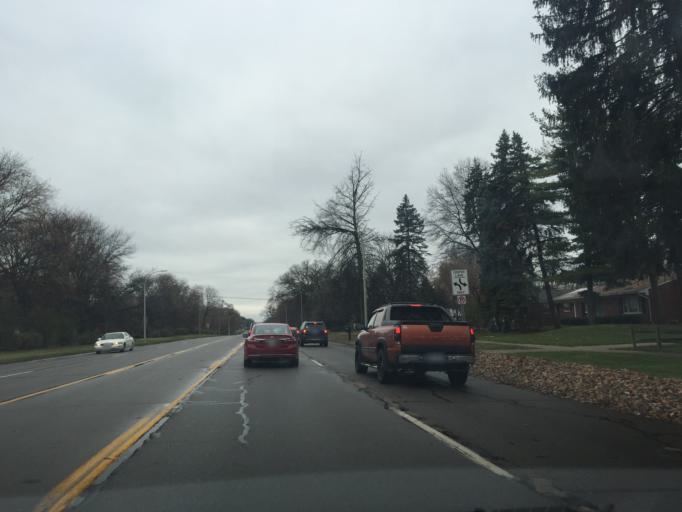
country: US
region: Michigan
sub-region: Wayne County
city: Redford
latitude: 42.4188
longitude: -83.3355
